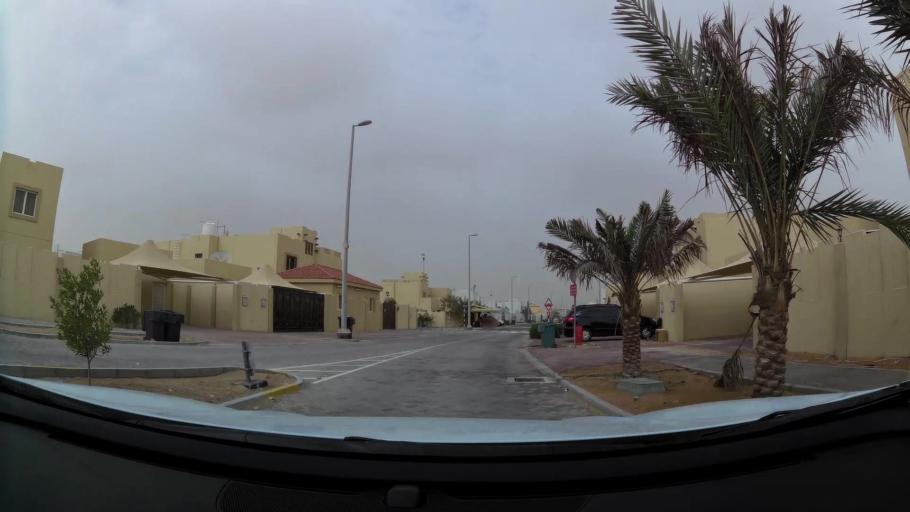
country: AE
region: Abu Dhabi
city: Abu Dhabi
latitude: 24.4545
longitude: 54.7119
